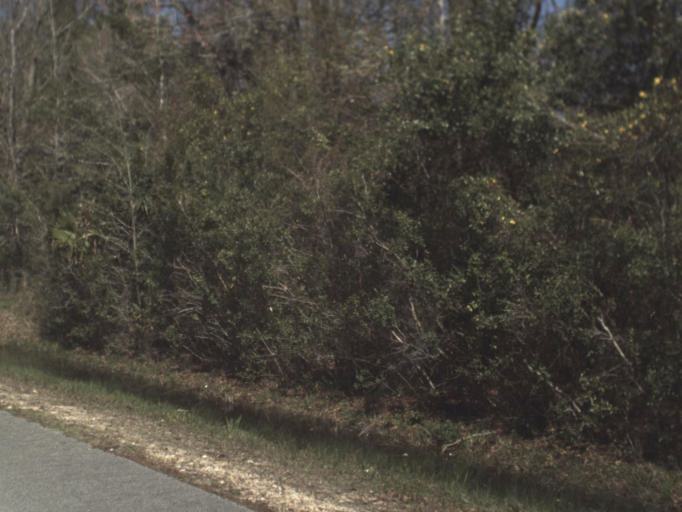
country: US
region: Florida
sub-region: Leon County
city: Woodville
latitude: 30.1842
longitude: -84.2135
